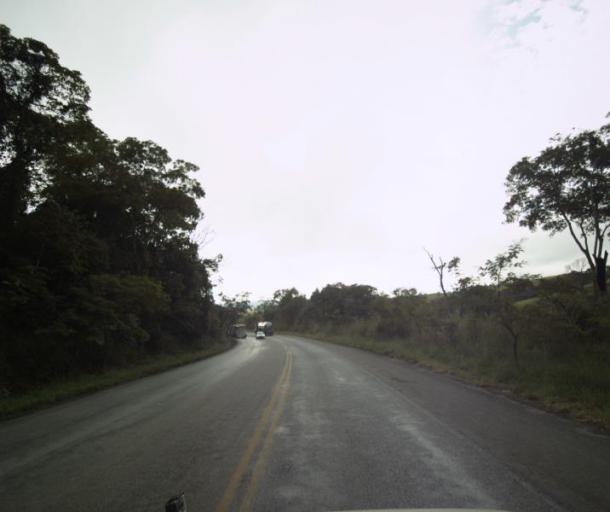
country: BR
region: Goias
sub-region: Pirenopolis
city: Pirenopolis
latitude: -15.7536
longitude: -48.7295
